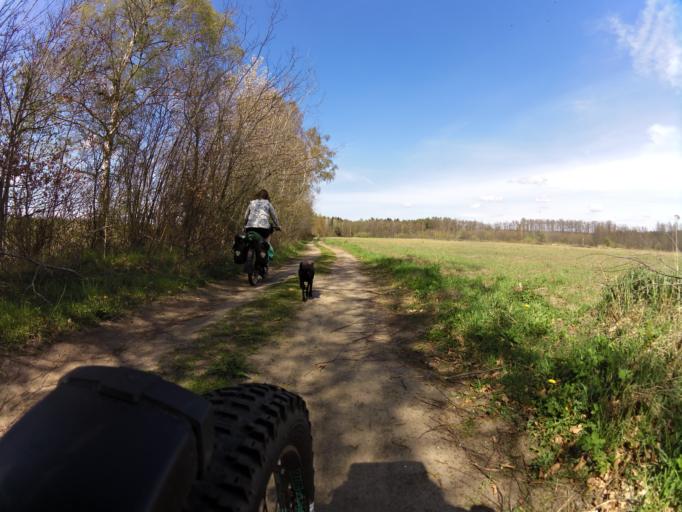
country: PL
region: West Pomeranian Voivodeship
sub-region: Powiat lobeski
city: Resko
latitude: 53.8028
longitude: 15.4444
